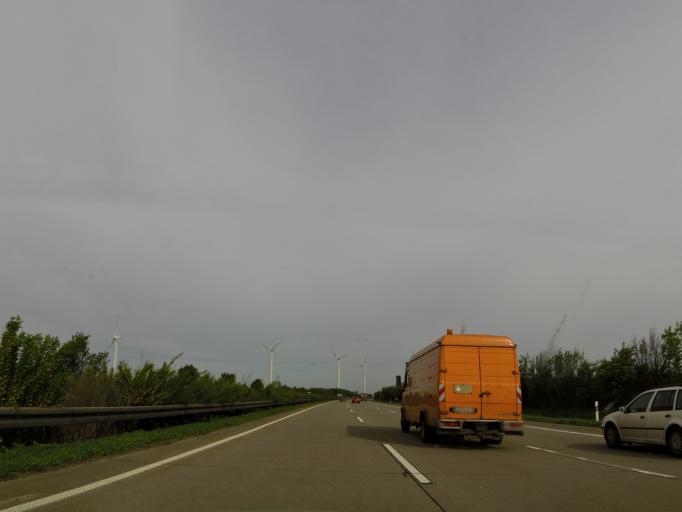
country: DE
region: Lower Saxony
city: Harsum
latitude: 52.1955
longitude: 9.9480
